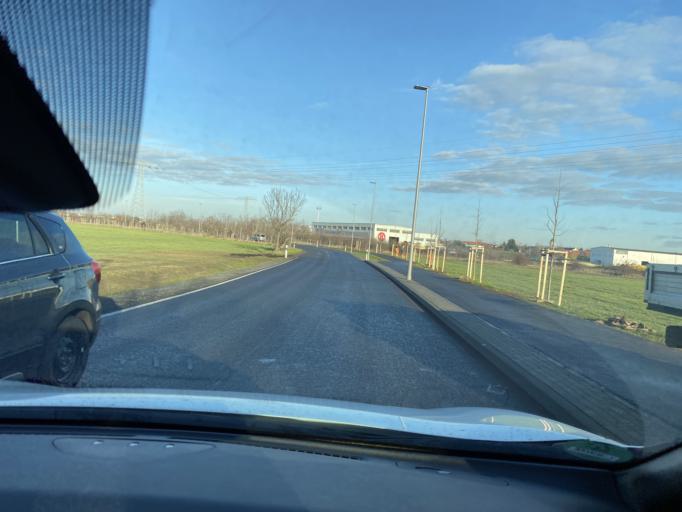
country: DE
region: Saxony
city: Markranstadt
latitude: 51.3457
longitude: 12.2842
